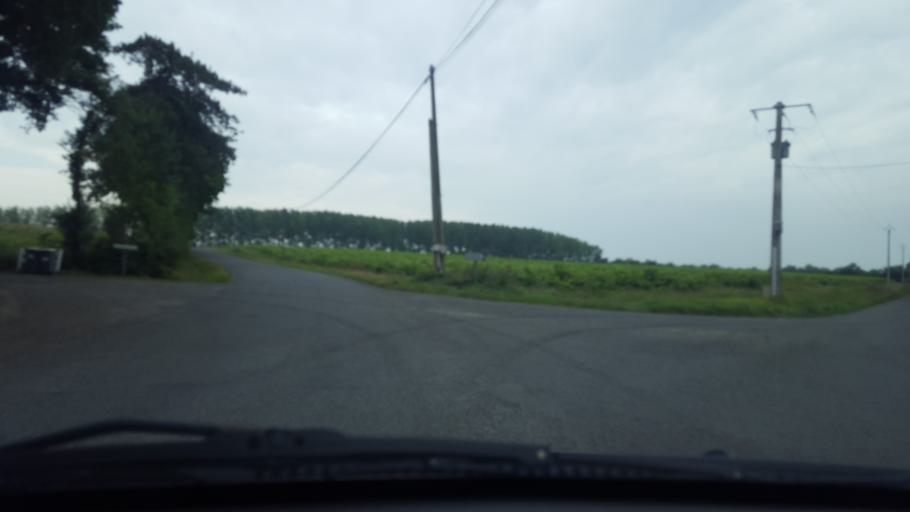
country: FR
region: Pays de la Loire
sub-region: Departement de la Loire-Atlantique
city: Saint-Philbert-de-Grand-Lieu
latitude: 47.0172
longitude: -1.6338
